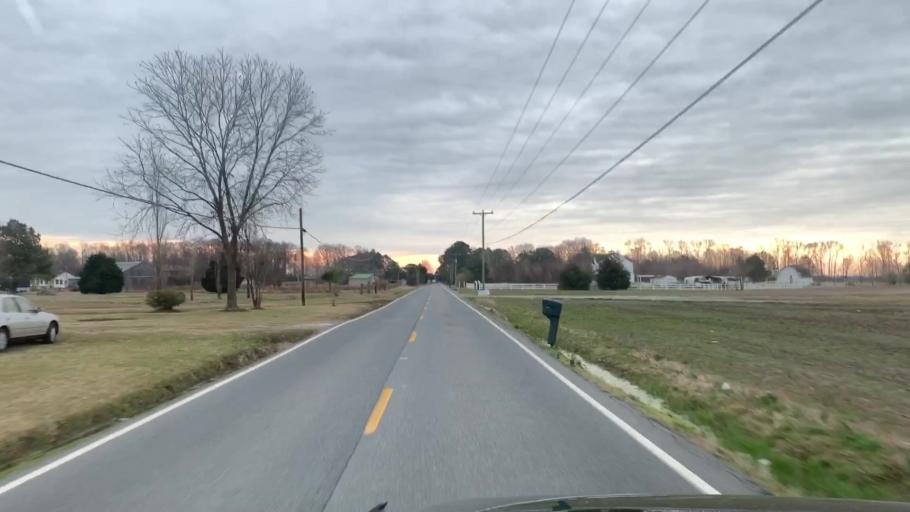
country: US
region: North Carolina
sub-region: Currituck County
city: Moyock
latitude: 36.6262
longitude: -76.1644
